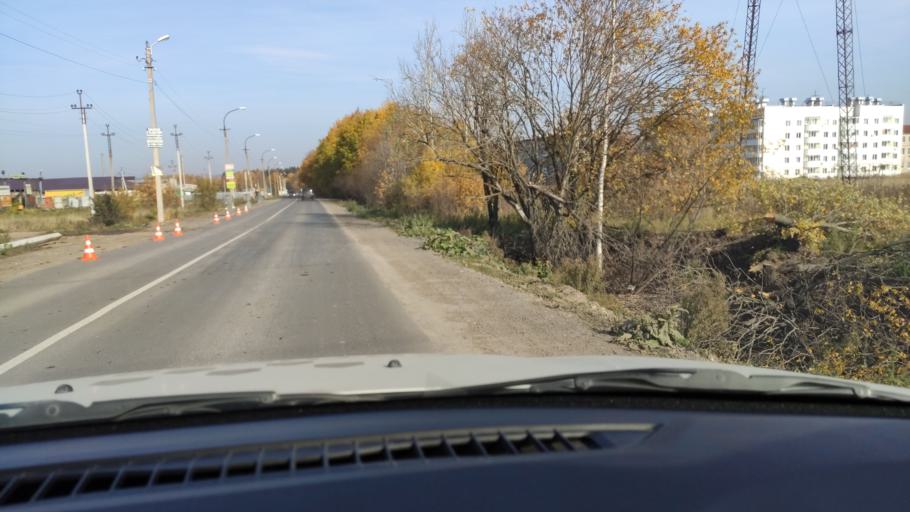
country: RU
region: Perm
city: Sylva
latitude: 58.0264
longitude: 56.7387
